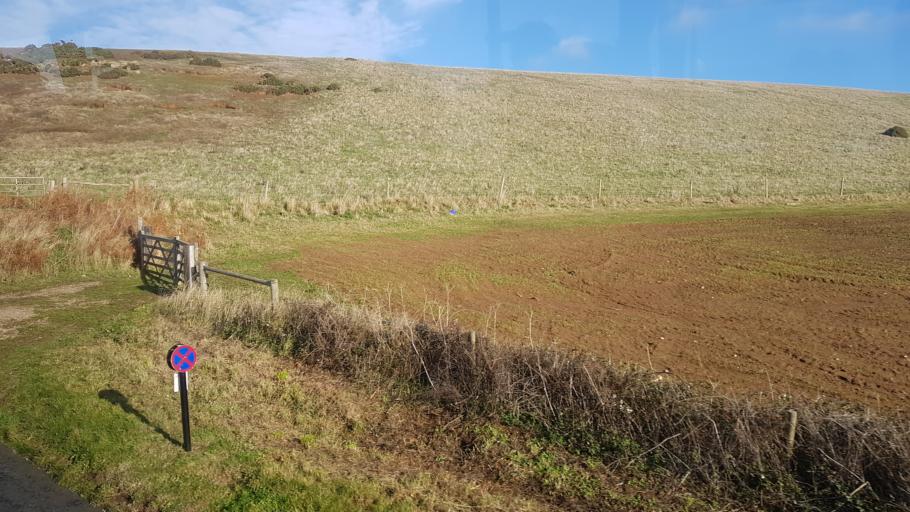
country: GB
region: England
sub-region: Isle of Wight
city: Freshwater
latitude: 50.6608
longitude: -1.4711
